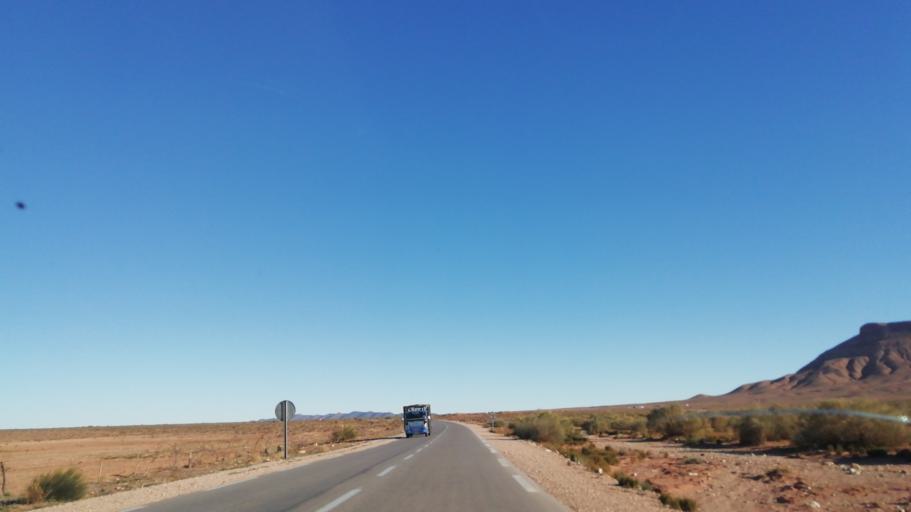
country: DZ
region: El Bayadh
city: El Abiodh Sidi Cheikh
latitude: 33.1130
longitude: 0.2506
